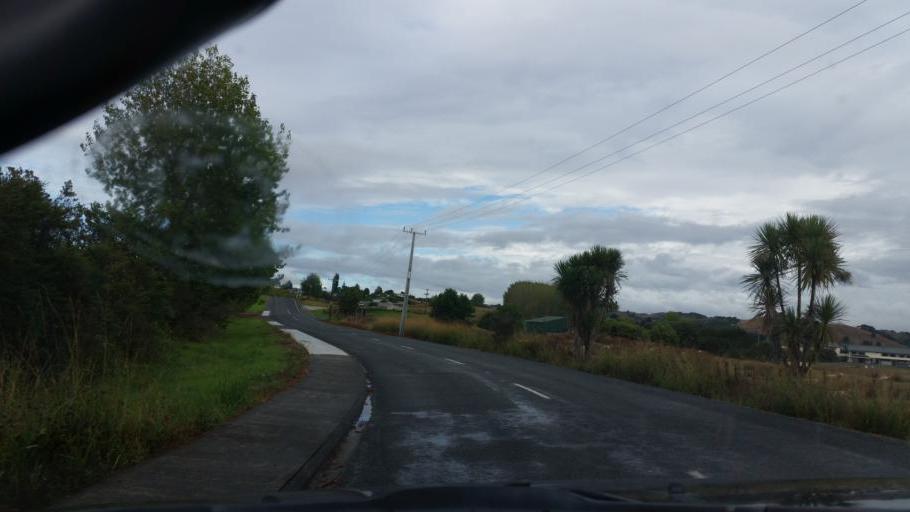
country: NZ
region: Northland
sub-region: Whangarei
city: Ruakaka
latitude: -36.1143
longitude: 174.3655
